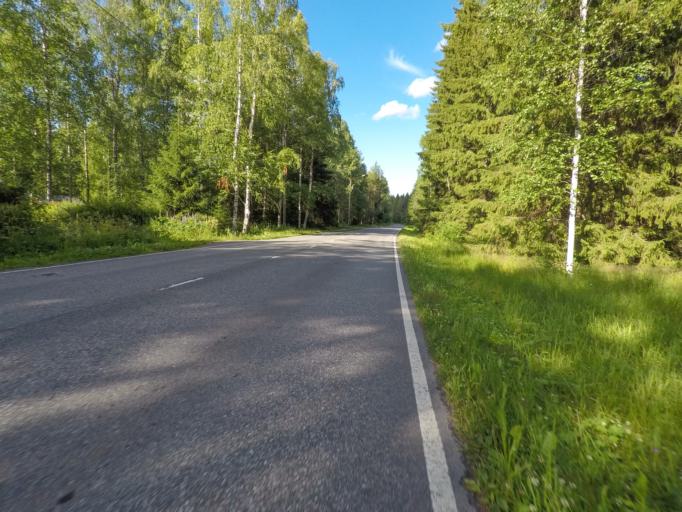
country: FI
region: South Karelia
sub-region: Imatra
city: Imatra
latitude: 61.1457
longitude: 28.7489
